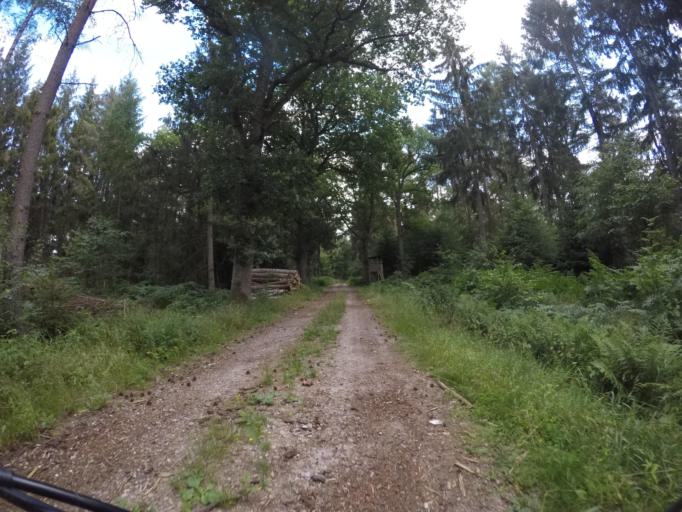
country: DE
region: Lower Saxony
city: Neu Darchau
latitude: 53.2838
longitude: 10.9736
